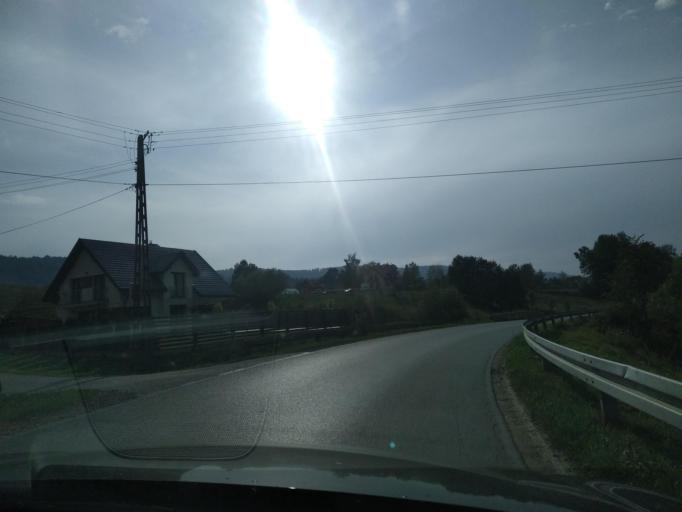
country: PL
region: Subcarpathian Voivodeship
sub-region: Powiat sanocki
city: Tyrawa Woloska
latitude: 49.5389
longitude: 22.4150
